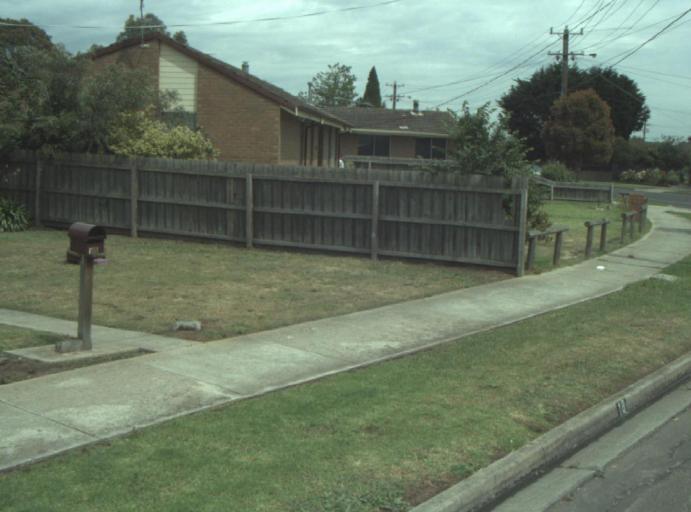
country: AU
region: Victoria
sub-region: Greater Geelong
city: Breakwater
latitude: -38.1763
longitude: 144.3923
